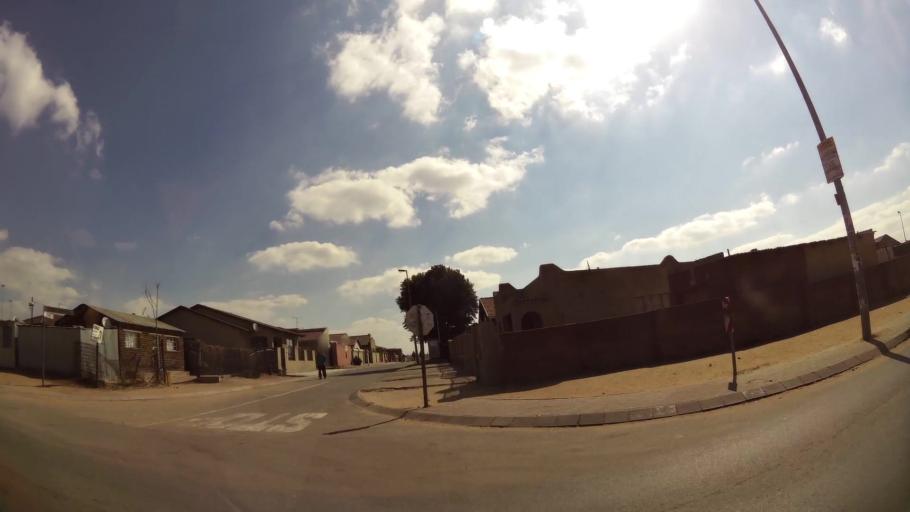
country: ZA
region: Gauteng
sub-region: Ekurhuleni Metropolitan Municipality
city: Tembisa
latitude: -26.0196
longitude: 28.1935
